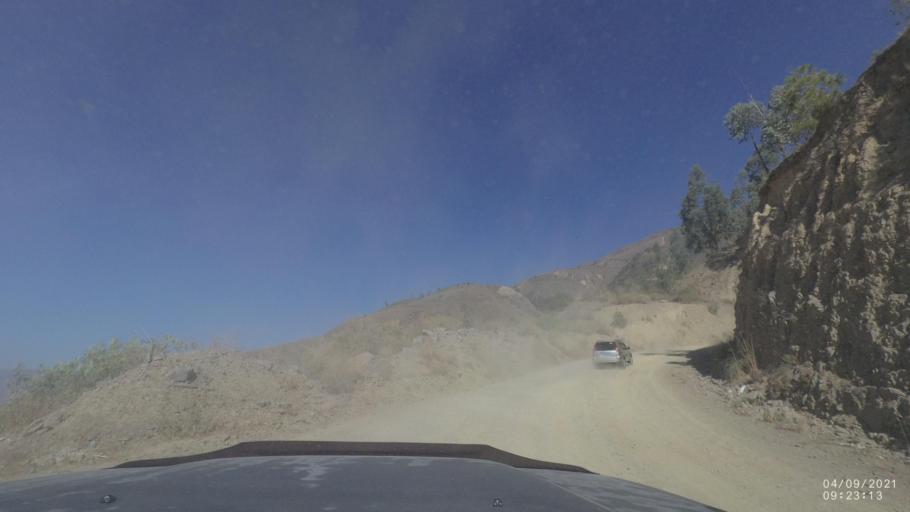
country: BO
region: Cochabamba
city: Sipe Sipe
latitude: -17.3639
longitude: -66.3669
